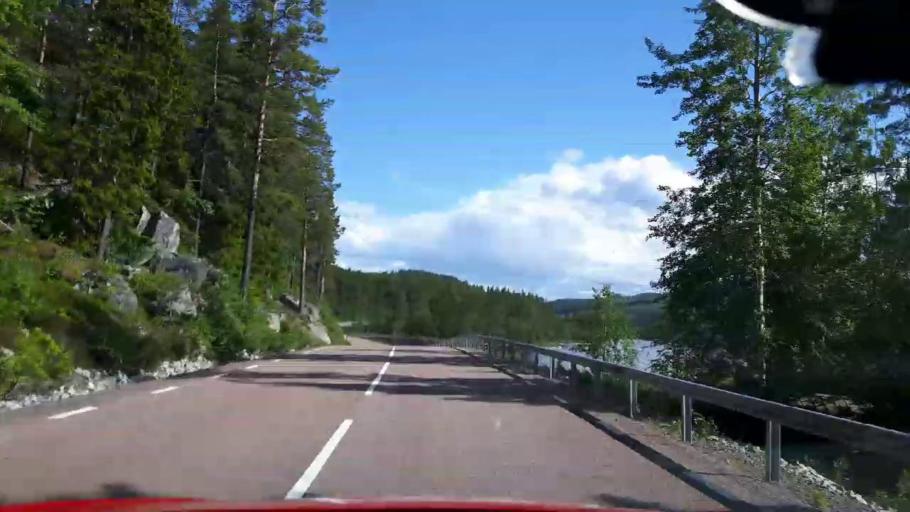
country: SE
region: Jaemtland
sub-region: Krokoms Kommun
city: Valla
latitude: 64.0301
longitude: 14.1929
